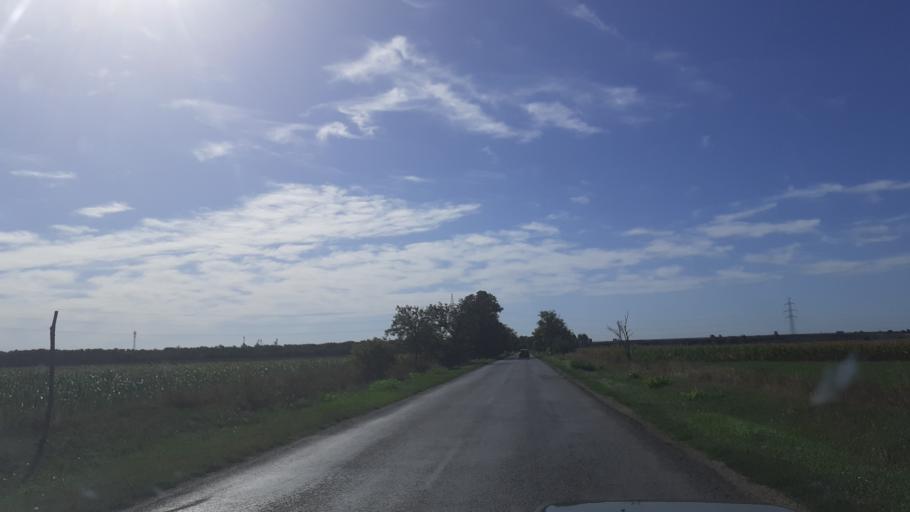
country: HU
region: Fejer
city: Ivancsa
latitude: 47.1848
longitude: 18.8009
